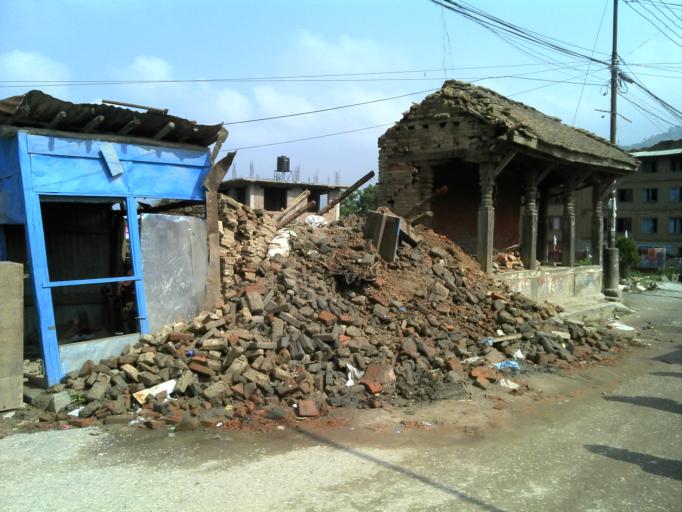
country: NP
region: Central Region
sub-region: Bagmati Zone
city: Nagarkot
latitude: 27.7278
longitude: 85.4615
